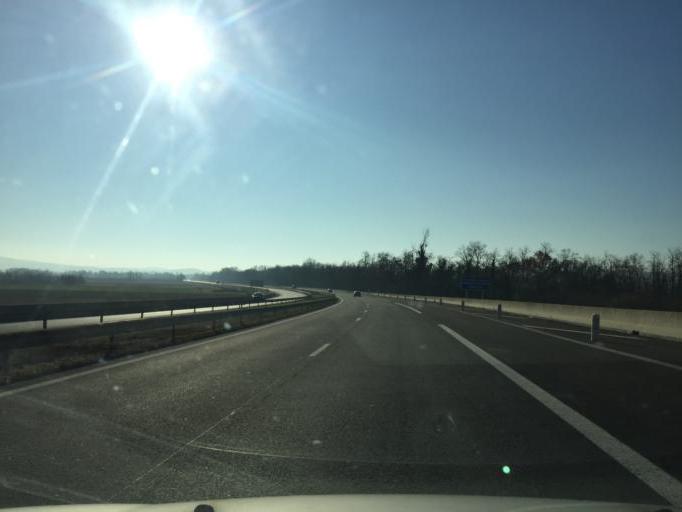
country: FR
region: Rhone-Alpes
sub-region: Departement du Rhone
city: Anse
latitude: 45.9258
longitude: 4.7255
